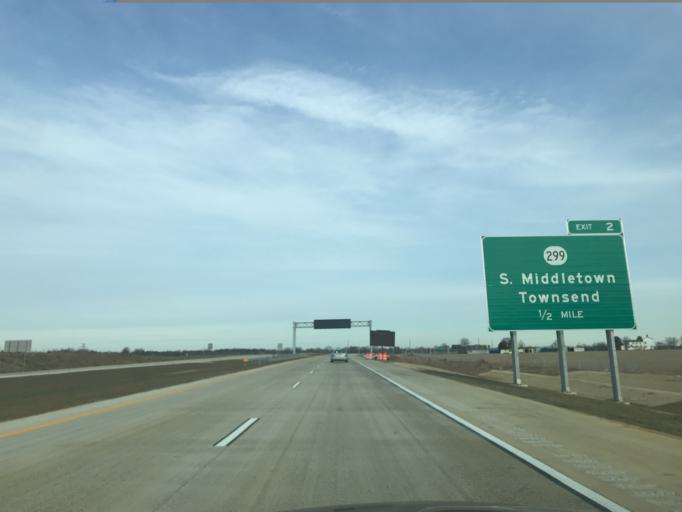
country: US
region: Delaware
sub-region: New Castle County
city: Middletown
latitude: 39.4350
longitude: -75.7590
